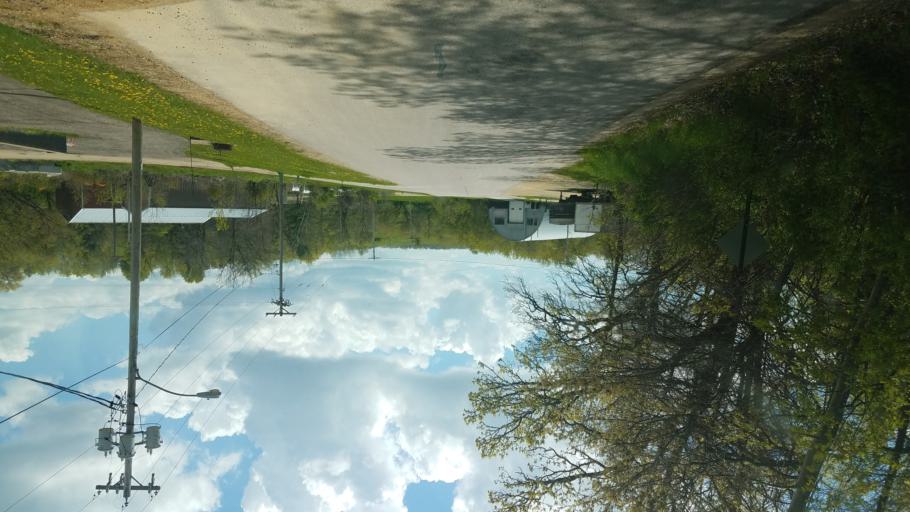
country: US
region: Wisconsin
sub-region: Vernon County
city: Hillsboro
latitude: 43.6511
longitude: -90.3330
